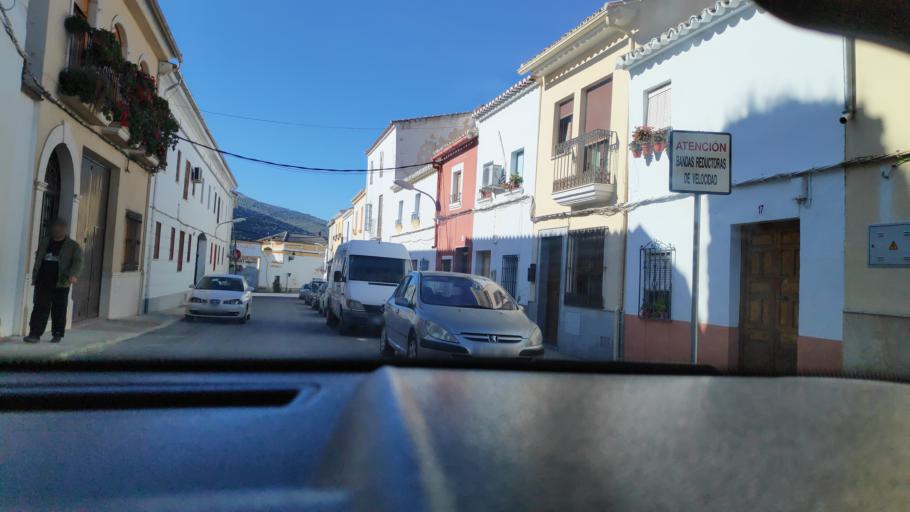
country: ES
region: Andalusia
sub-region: Province of Cordoba
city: Baena
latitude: 37.6122
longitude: -4.3224
